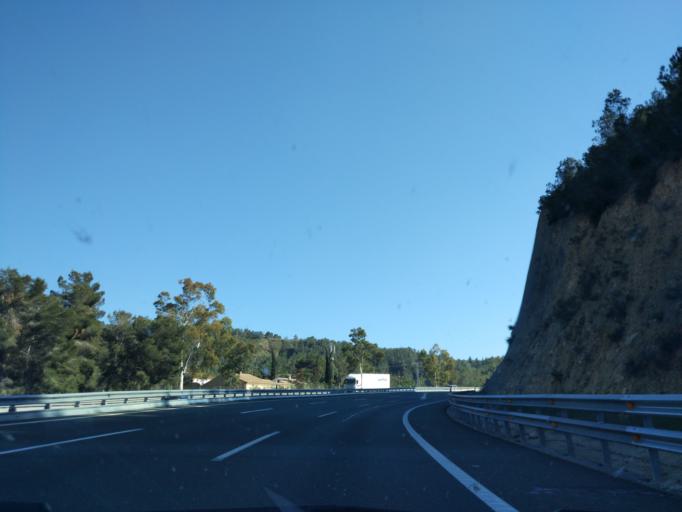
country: ES
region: Murcia
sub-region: Murcia
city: Murcia
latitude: 37.8997
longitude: -1.1427
